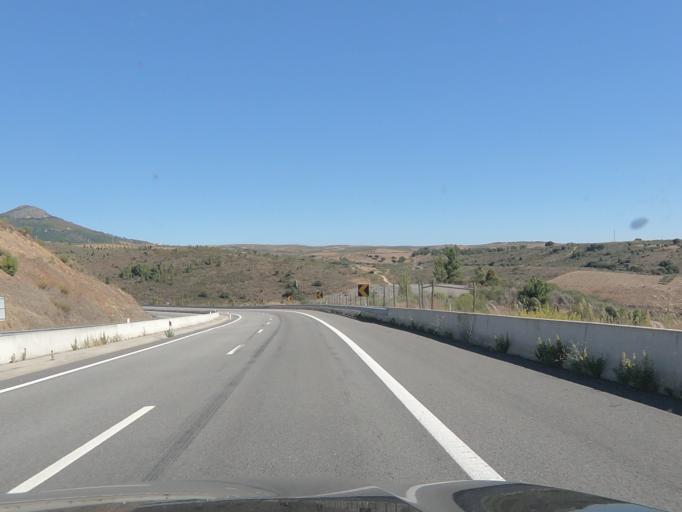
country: PT
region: Vila Real
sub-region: Murca
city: Murca
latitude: 41.4230
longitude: -7.3656
